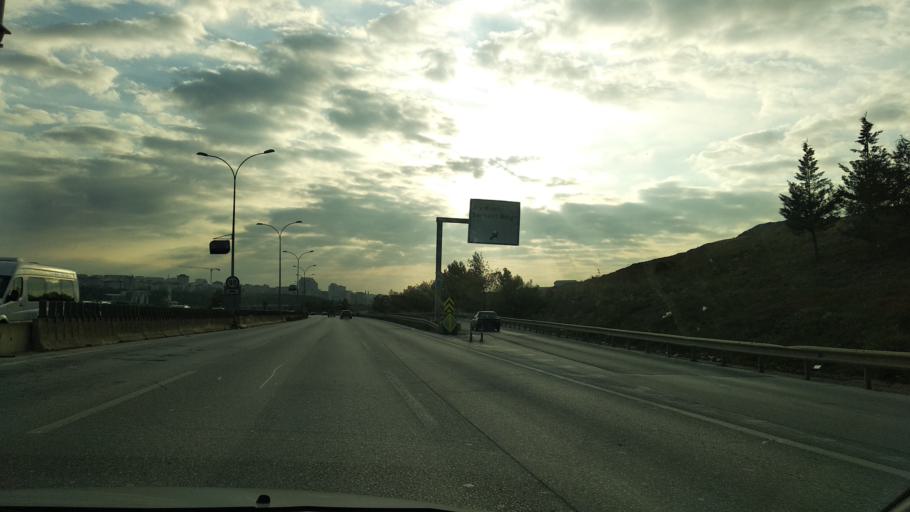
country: TR
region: Istanbul
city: Icmeler
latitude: 40.8836
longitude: 29.3198
